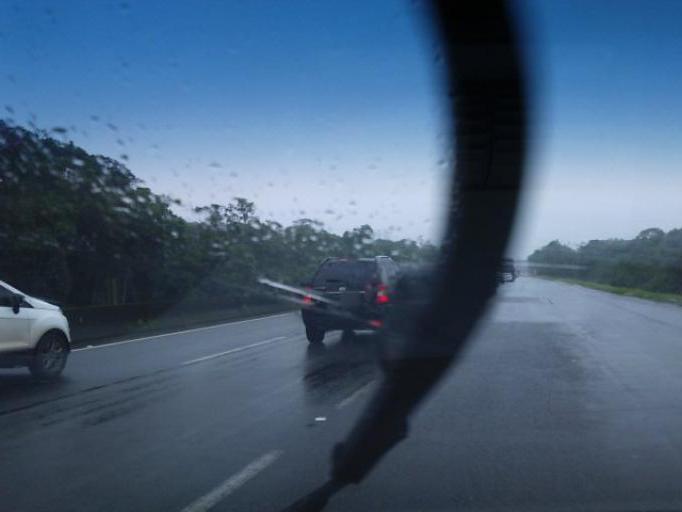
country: BR
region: Santa Catarina
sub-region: Joinville
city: Joinville
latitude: -26.0634
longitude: -48.8601
